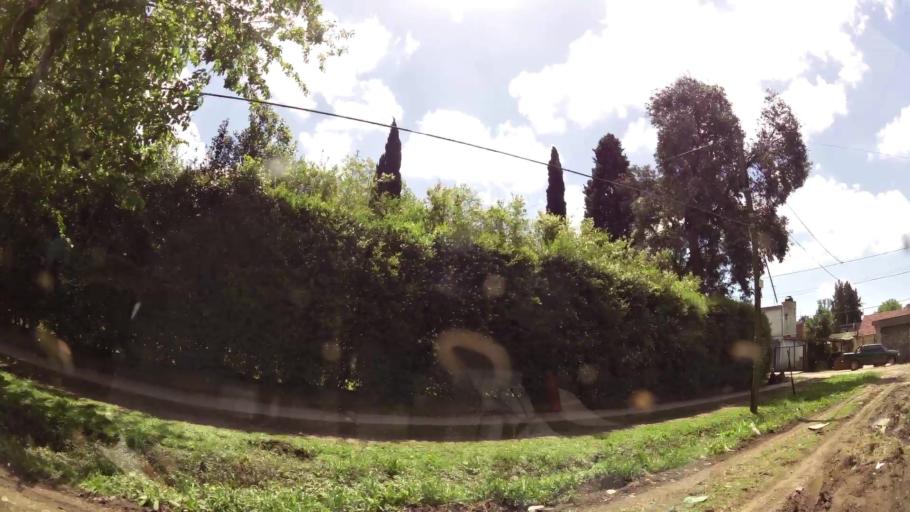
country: AR
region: Buenos Aires
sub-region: Partido de Quilmes
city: Quilmes
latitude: -34.8135
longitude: -58.2354
